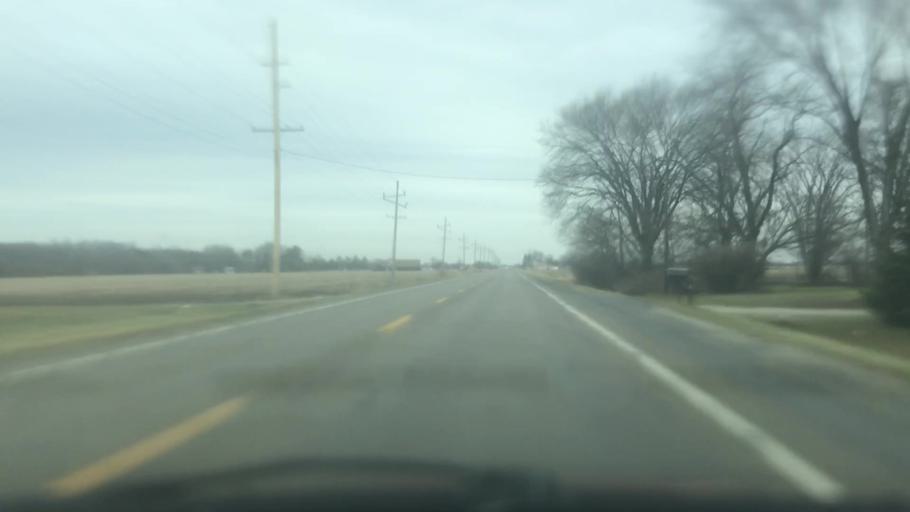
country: US
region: Indiana
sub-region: Porter County
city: Kouts
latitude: 41.3278
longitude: -87.0260
